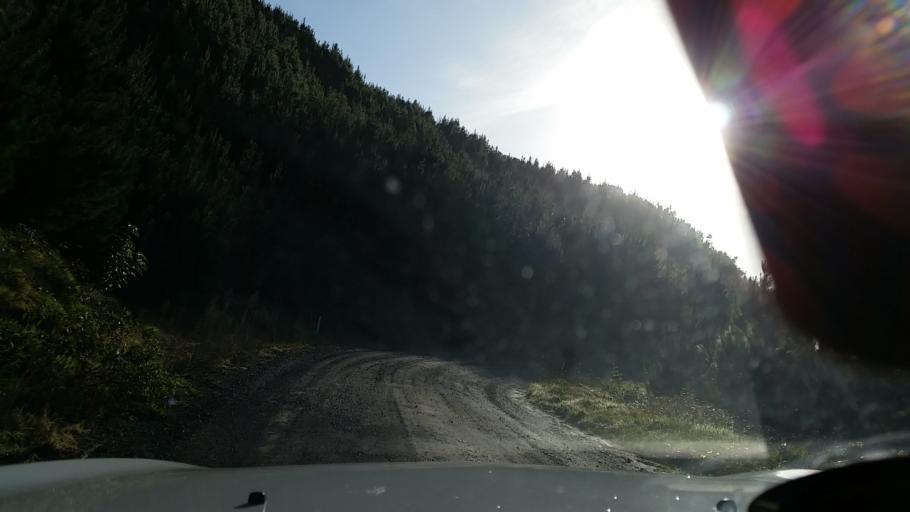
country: NZ
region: Bay of Plenty
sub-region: Kawerau District
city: Kawerau
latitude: -38.0317
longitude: 176.5541
